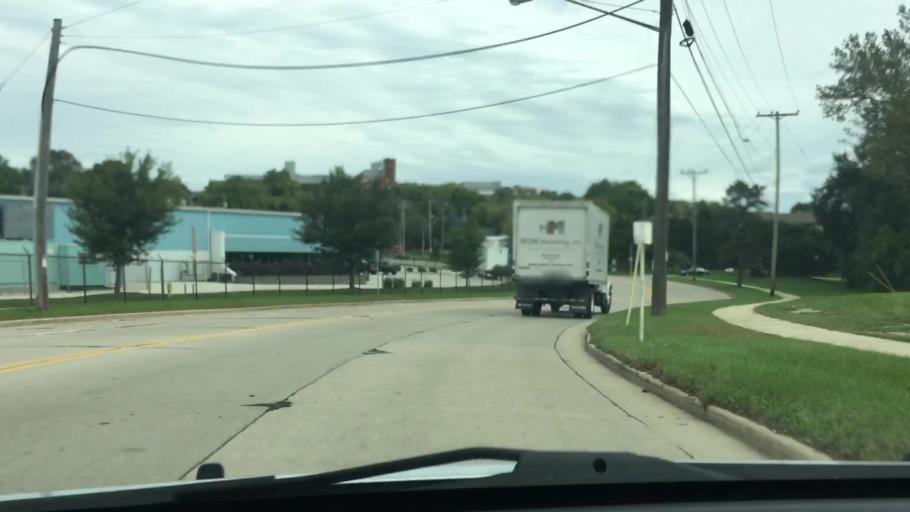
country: US
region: Wisconsin
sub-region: Waukesha County
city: Waukesha
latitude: 43.0055
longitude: -88.2436
